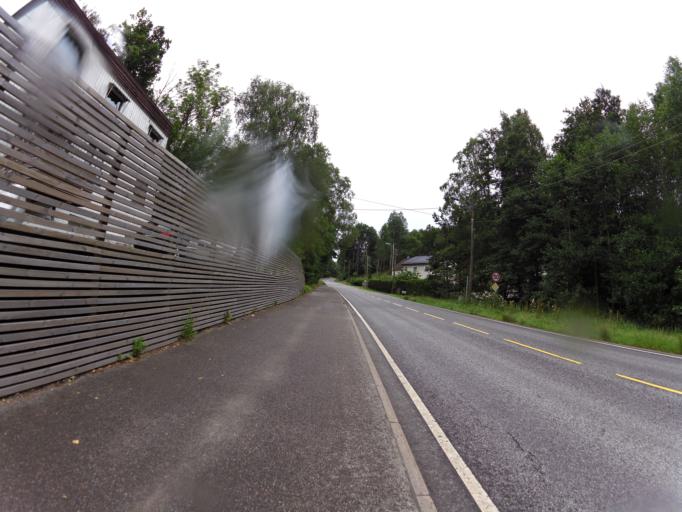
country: NO
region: Ostfold
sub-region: Moss
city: Moss
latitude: 59.4690
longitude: 10.6898
